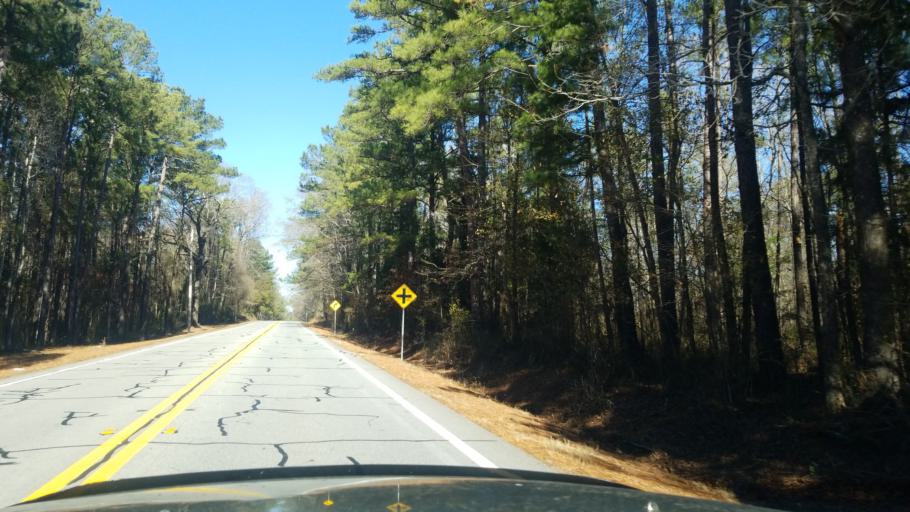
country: US
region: Georgia
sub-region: Harris County
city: Hamilton
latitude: 32.6731
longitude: -84.8590
